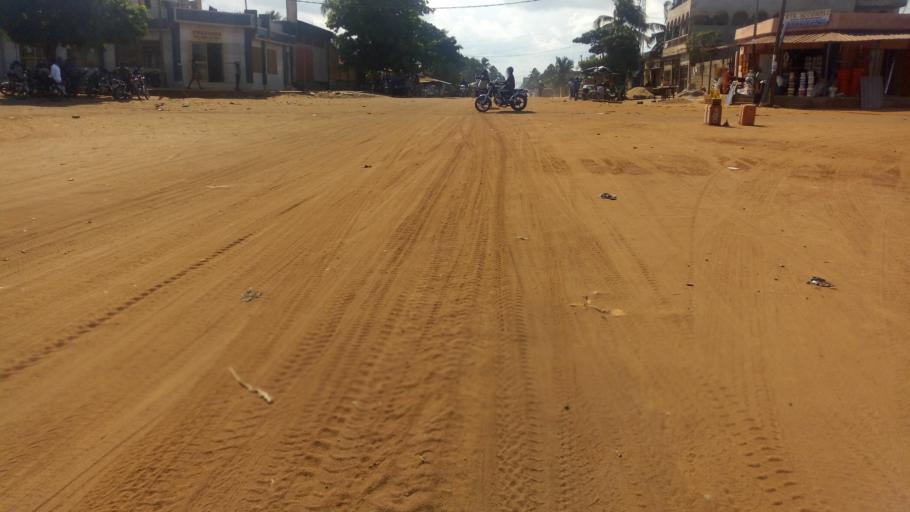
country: TG
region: Maritime
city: Lome
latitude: 6.2272
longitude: 1.1853
